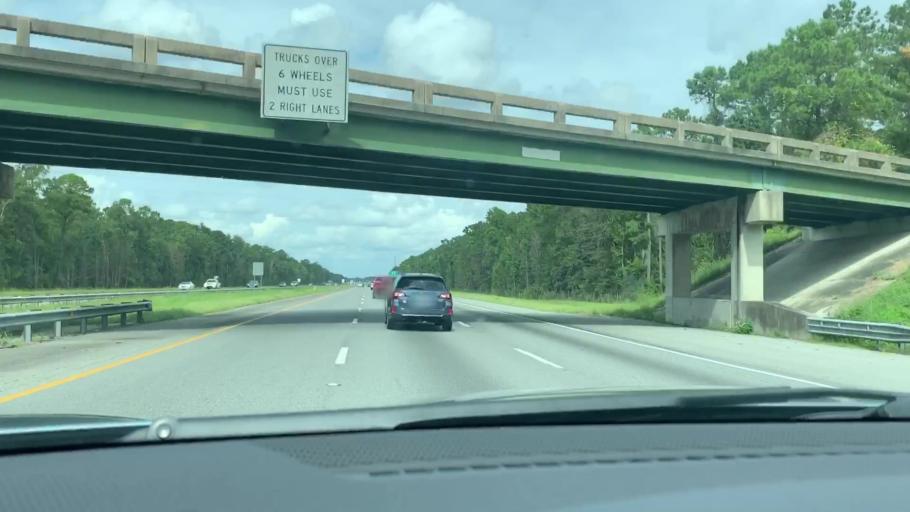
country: US
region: Georgia
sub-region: Liberty County
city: Midway
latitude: 31.6338
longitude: -81.4048
